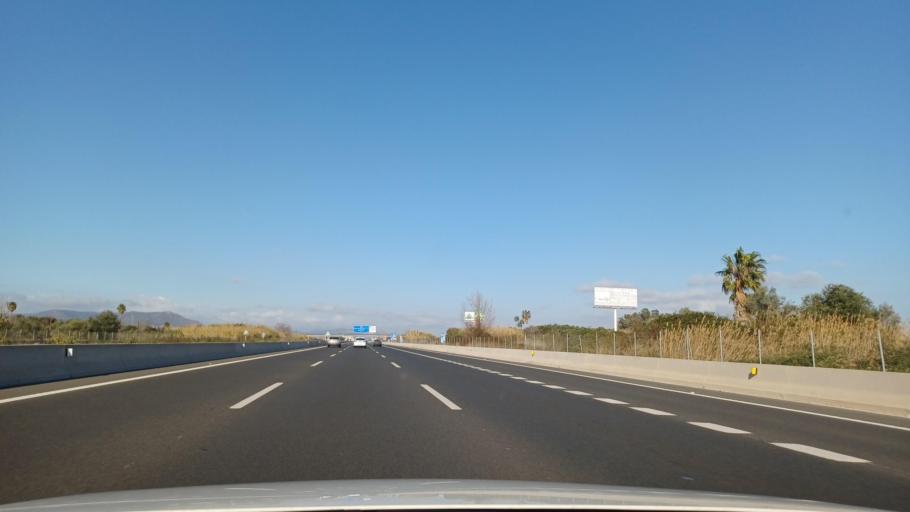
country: ES
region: Valencia
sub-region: Provincia de Valencia
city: Albuixech
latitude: 39.5631
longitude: -0.2963
